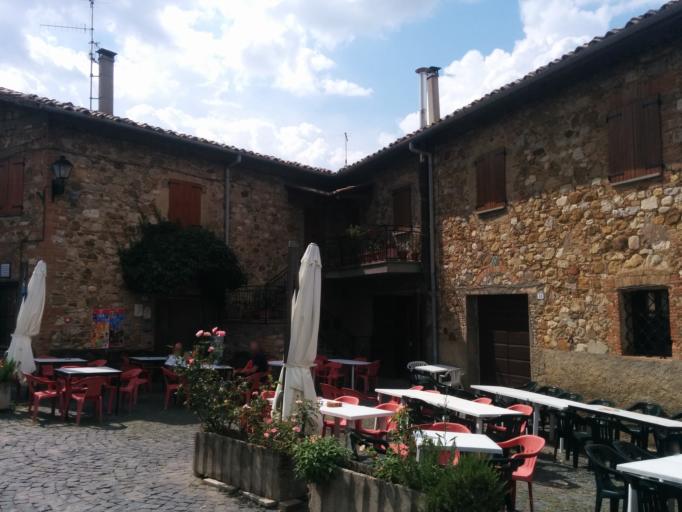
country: IT
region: Tuscany
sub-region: Provincia di Siena
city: San Casciano dei Bagni
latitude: 42.8226
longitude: 11.8719
